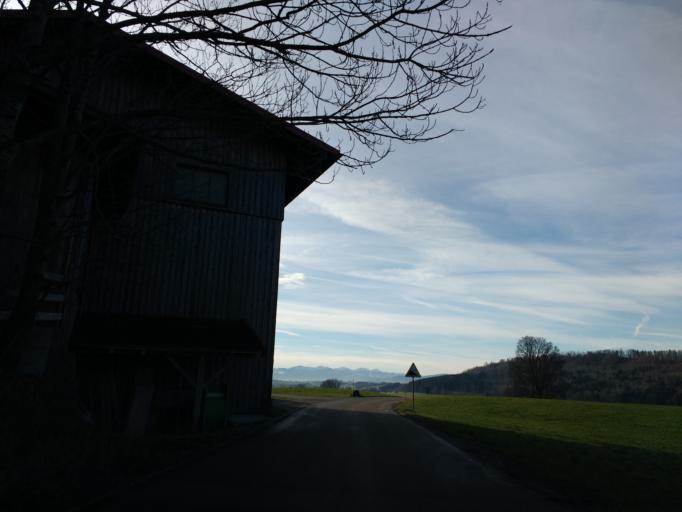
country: DE
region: Bavaria
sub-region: Swabia
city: Wildpoldsried
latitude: 47.7818
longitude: 10.4054
